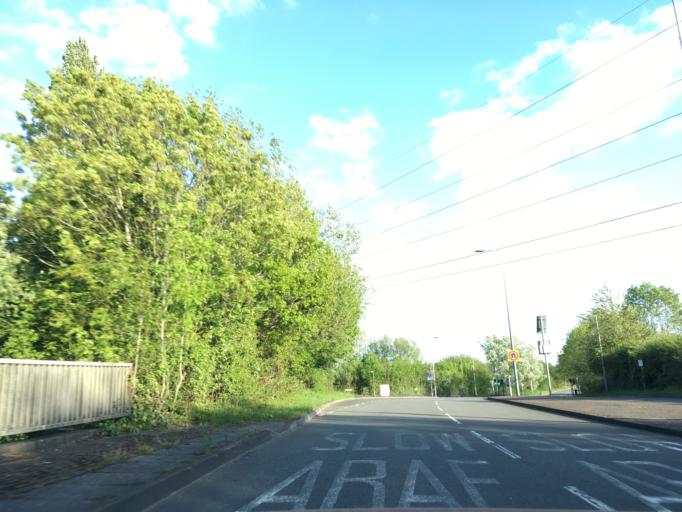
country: GB
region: Wales
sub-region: Newport
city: Marshfield
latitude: 51.5284
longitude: -3.0886
